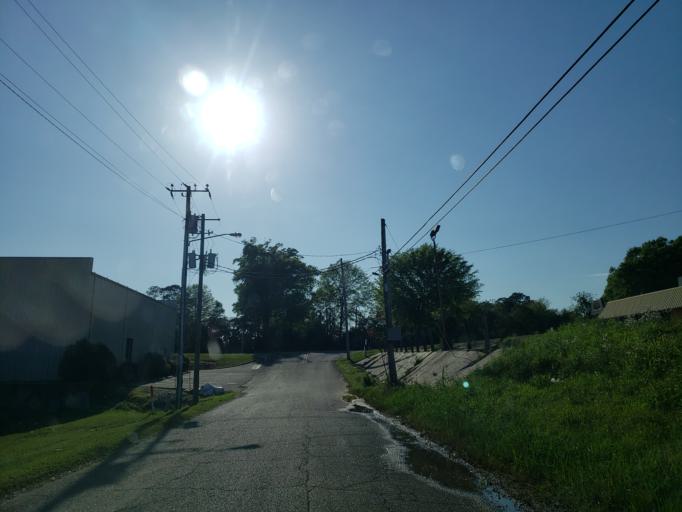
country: US
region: Mississippi
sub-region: Jones County
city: Laurel
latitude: 31.6957
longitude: -89.1458
